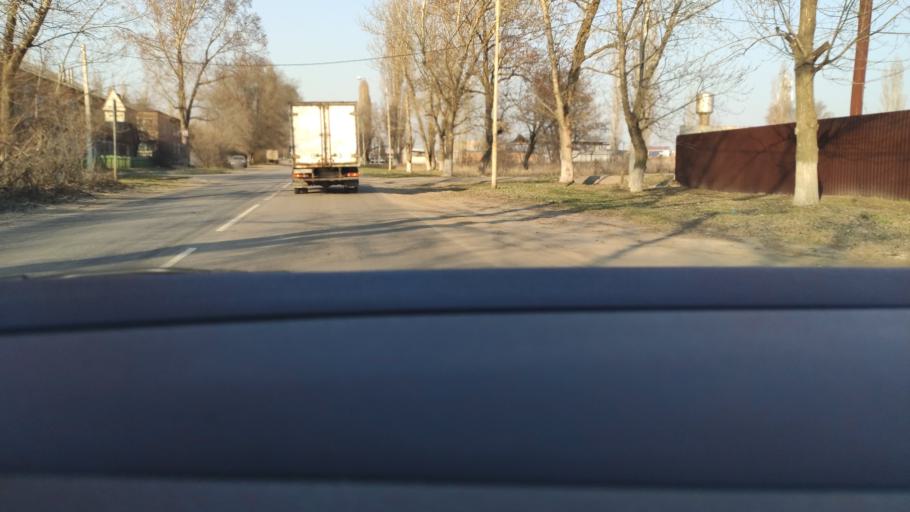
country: RU
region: Voronezj
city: Maslovka
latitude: 51.5819
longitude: 39.3169
